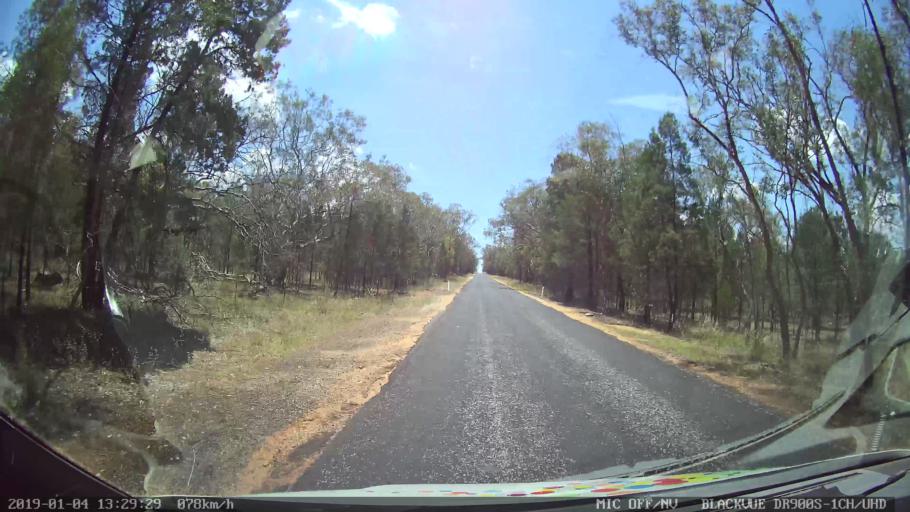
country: AU
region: New South Wales
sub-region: Parkes
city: Peak Hill
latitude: -32.6461
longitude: 148.5510
